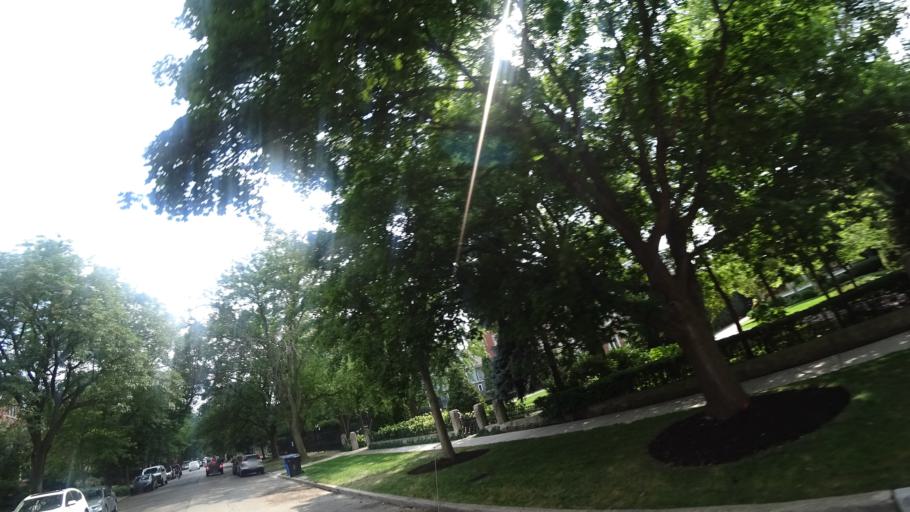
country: US
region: Illinois
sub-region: Cook County
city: Chicago
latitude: 41.8051
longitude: -87.5968
